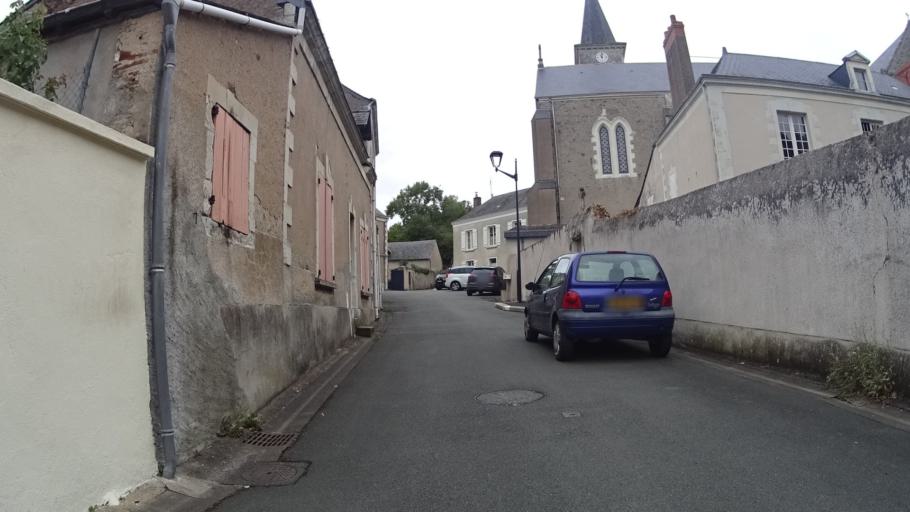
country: FR
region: Pays de la Loire
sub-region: Departement de Maine-et-Loire
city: La Possonniere
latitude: 47.3746
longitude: -0.6847
